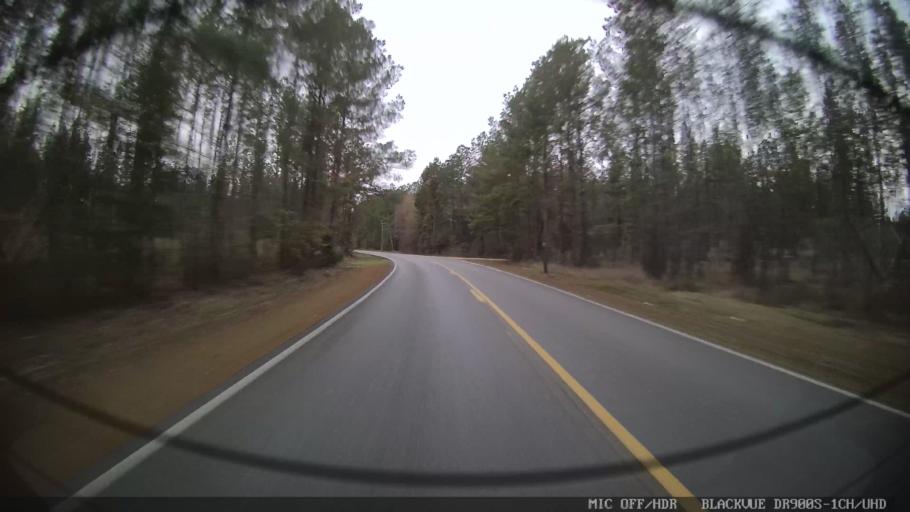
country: US
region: Mississippi
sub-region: Clarke County
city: Quitman
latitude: 32.0293
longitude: -88.8309
